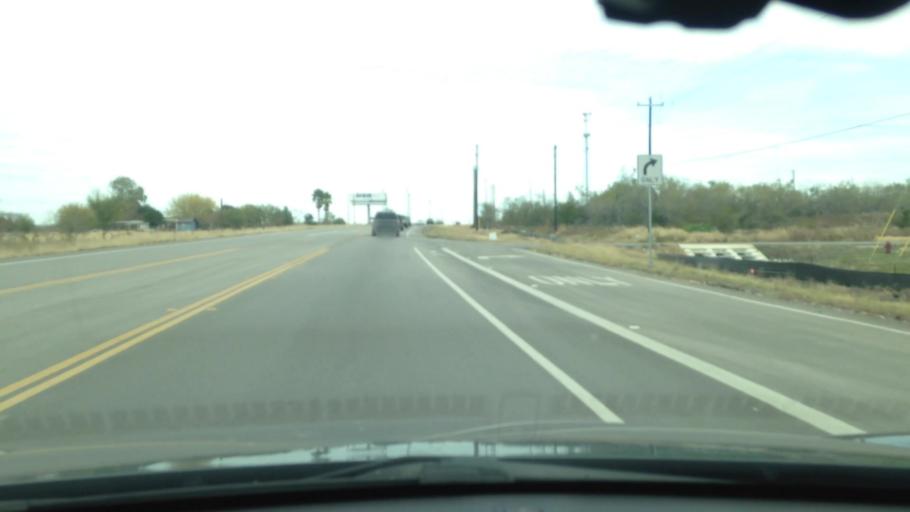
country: US
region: Texas
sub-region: Caldwell County
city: Uhland
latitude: 29.9884
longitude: -97.7577
